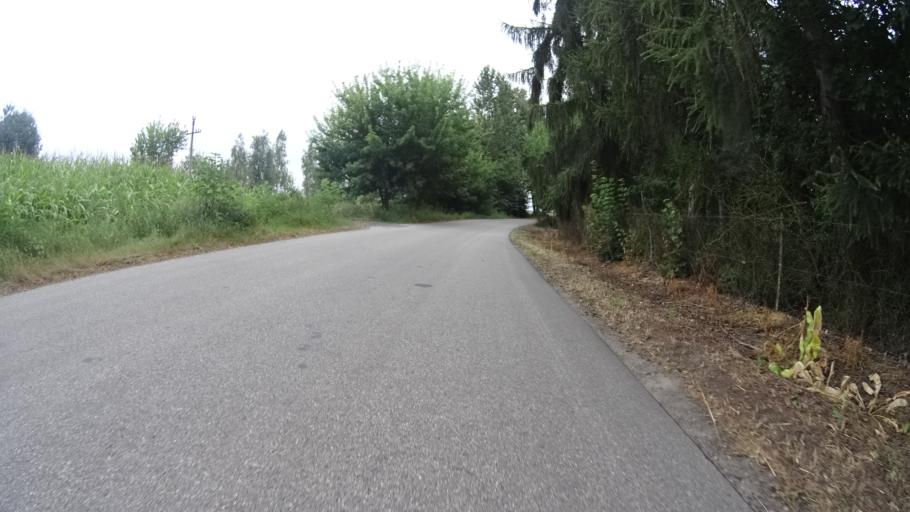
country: PL
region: Masovian Voivodeship
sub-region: Powiat grojecki
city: Goszczyn
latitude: 51.6851
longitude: 20.8614
